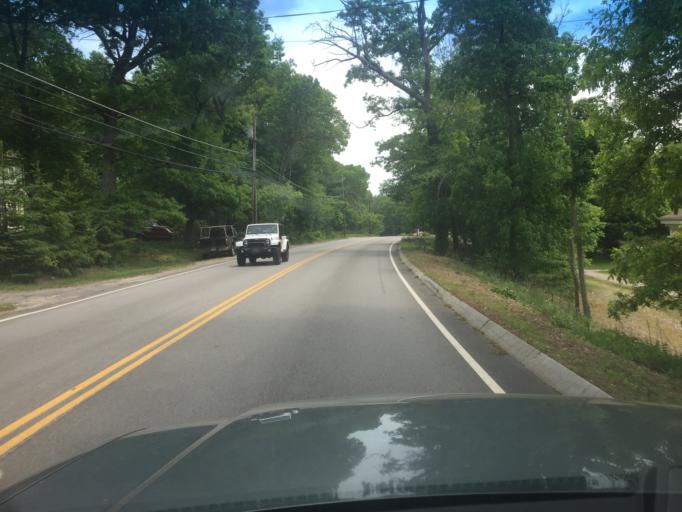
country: US
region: Massachusetts
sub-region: Norfolk County
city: Westwood
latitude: 42.2037
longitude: -71.2570
